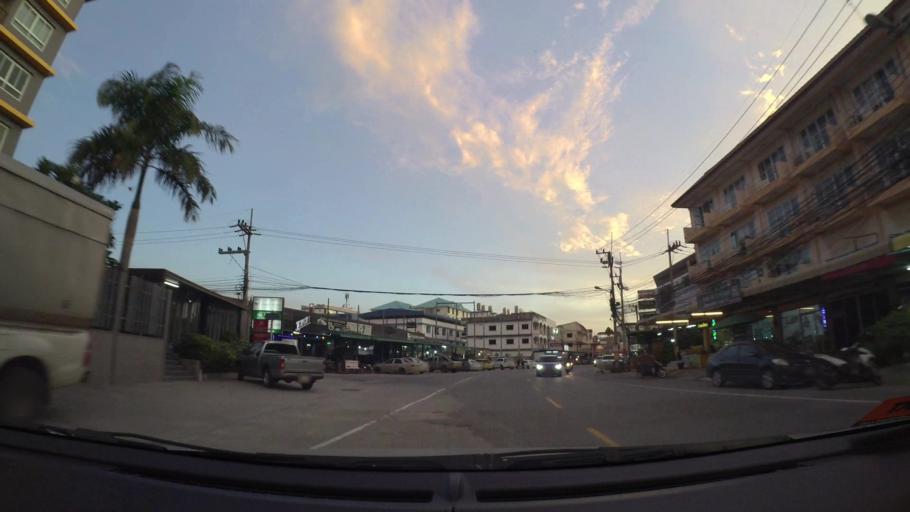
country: TH
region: Chon Buri
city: Chon Buri
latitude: 13.4197
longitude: 101.0026
